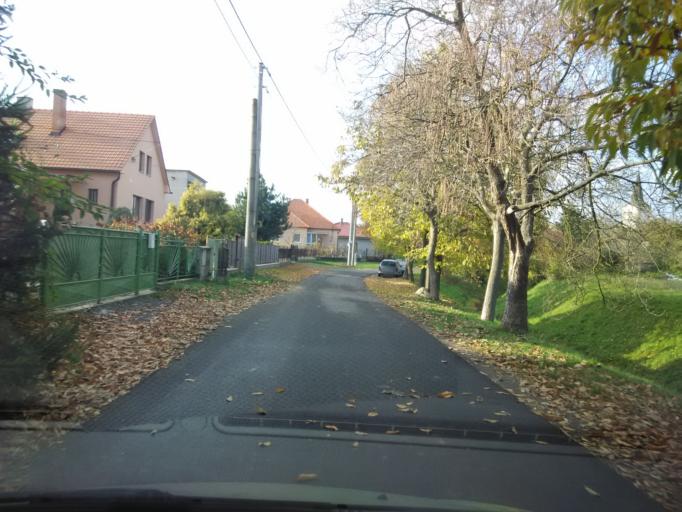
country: SK
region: Nitriansky
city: Tlmace
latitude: 48.3176
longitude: 18.5261
